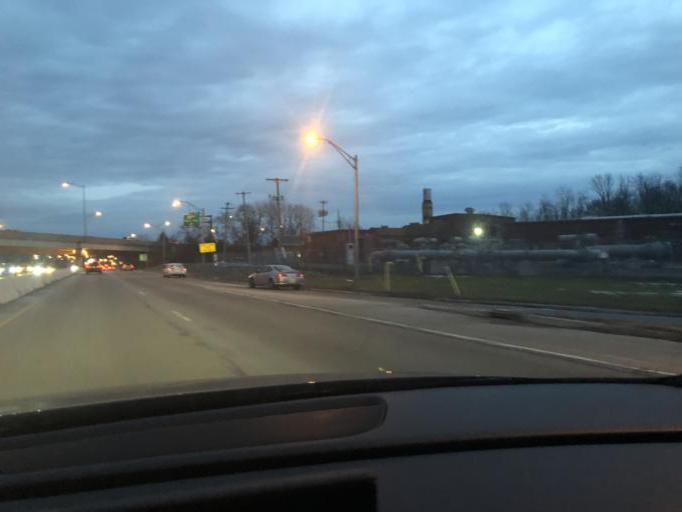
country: US
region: New Jersey
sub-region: Morris County
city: Madison
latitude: 40.7925
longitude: -74.4297
